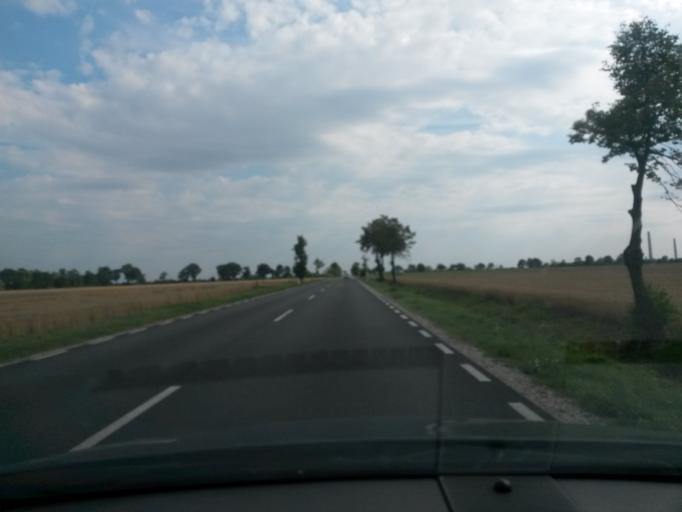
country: PL
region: Greater Poland Voivodeship
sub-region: Powiat gostynski
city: Krobia
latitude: 51.7209
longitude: 16.9485
